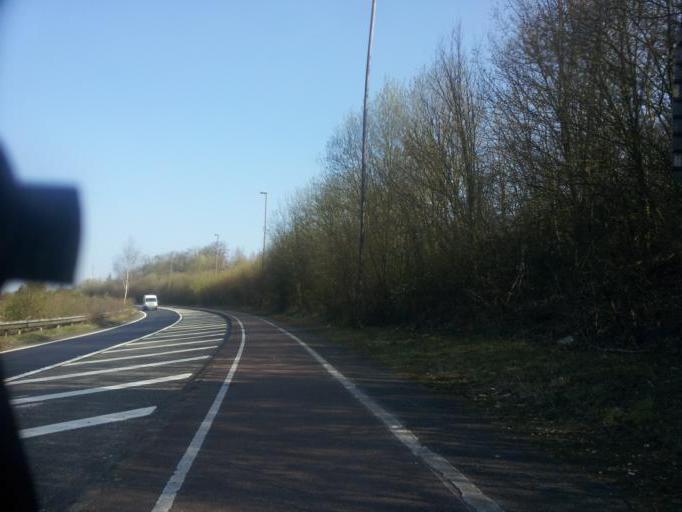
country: GB
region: England
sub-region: Medway
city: Cuxton
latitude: 51.3982
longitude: 0.4397
